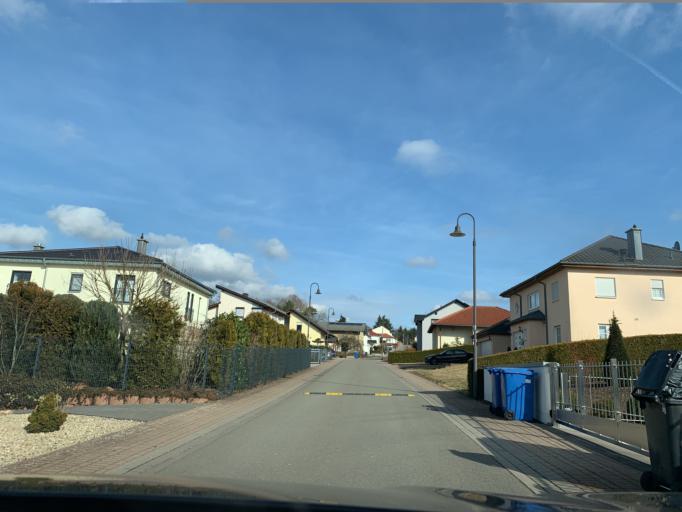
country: DE
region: Rheinland-Pfalz
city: Clausen
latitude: 49.2625
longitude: 7.6714
